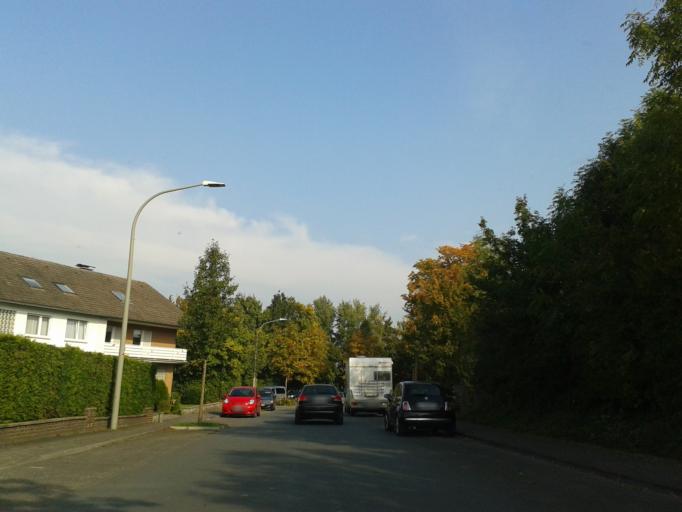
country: DE
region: North Rhine-Westphalia
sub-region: Regierungsbezirk Detmold
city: Salzkotten
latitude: 51.7139
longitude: 8.6323
